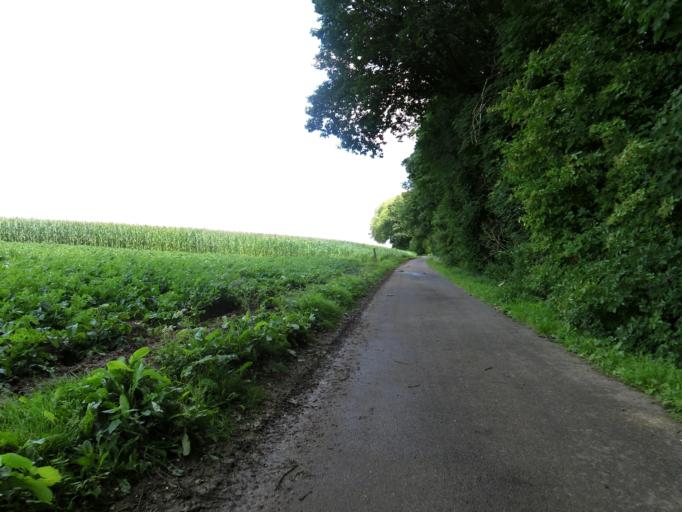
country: NL
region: Limburg
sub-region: Gemeente Voerendaal
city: Ubachsberg
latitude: 50.8316
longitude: 5.9184
